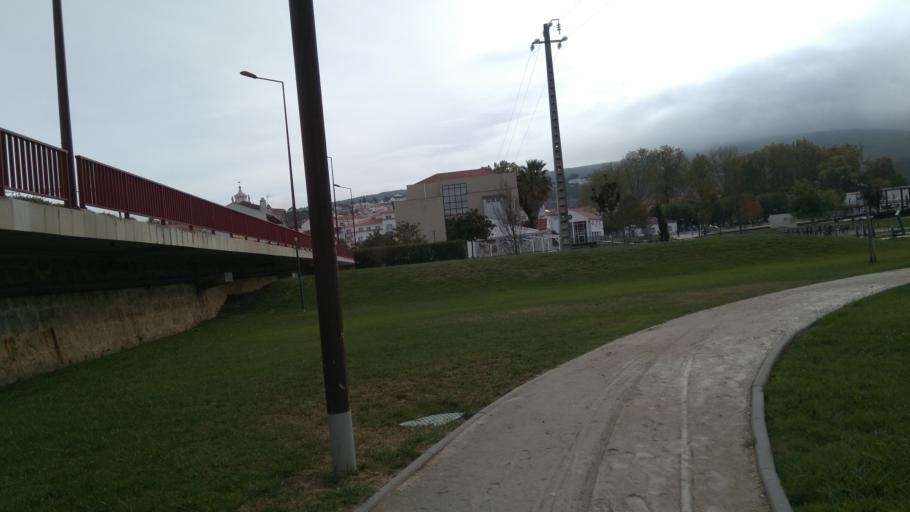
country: PT
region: Leiria
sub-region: Porto de Mos
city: Porto de Mos
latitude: 39.5994
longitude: -8.8222
